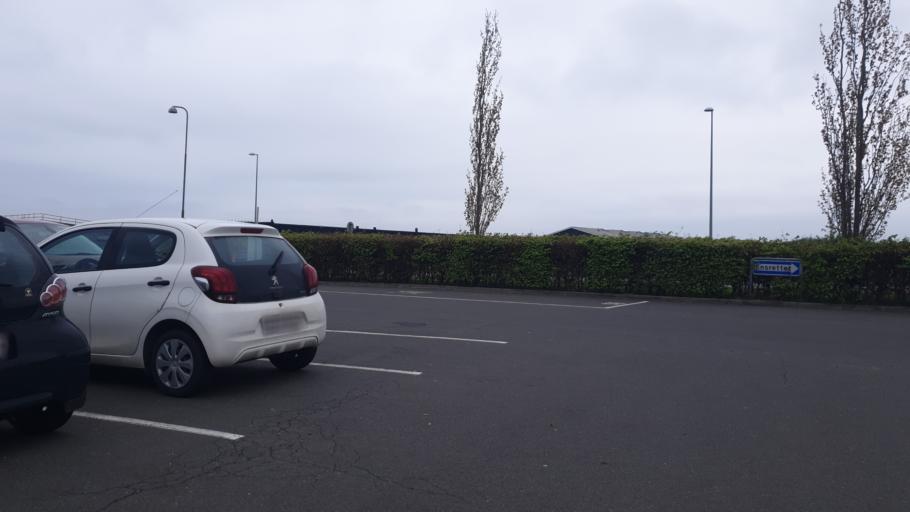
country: DK
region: Central Jutland
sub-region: Hedensted Kommune
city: Hedensted
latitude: 55.7810
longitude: 9.6907
